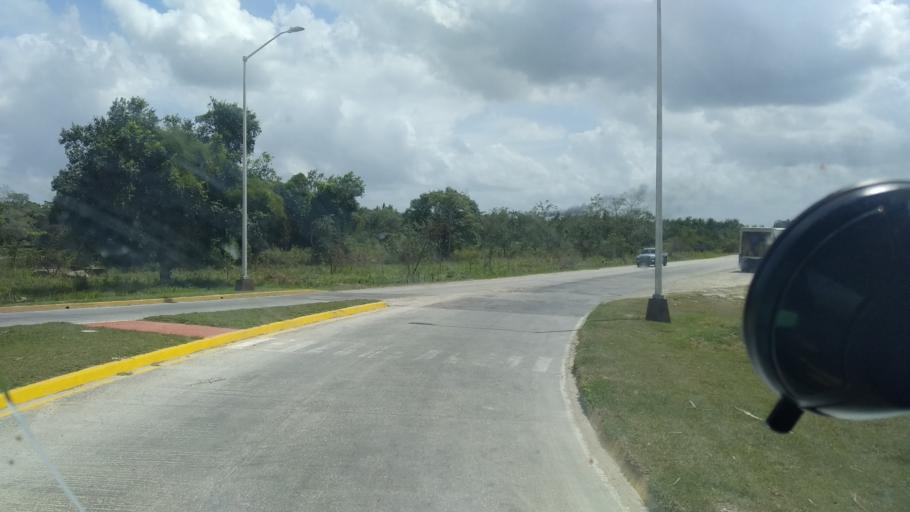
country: BZ
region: Orange Walk
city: Orange Walk
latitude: 18.0549
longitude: -88.5656
